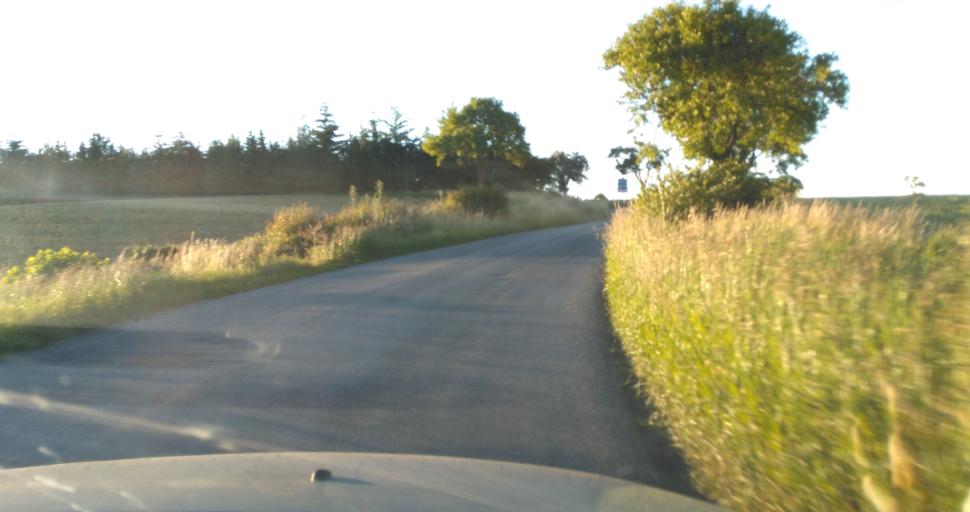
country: CZ
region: Central Bohemia
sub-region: Okres Beroun
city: Kraluv Dvur
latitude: 49.9116
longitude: 14.0339
